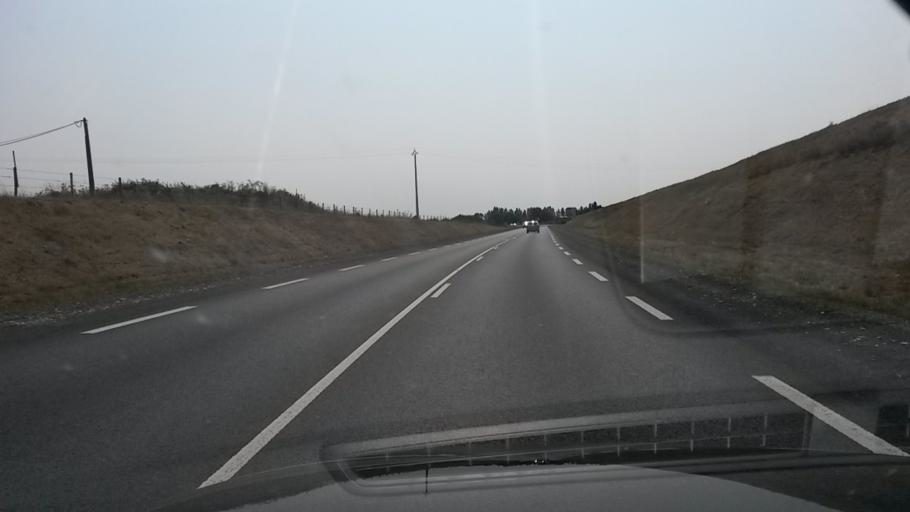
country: FR
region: Pays de la Loire
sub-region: Departement de la Loire-Atlantique
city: Mesanger
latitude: 47.4181
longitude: -1.1856
